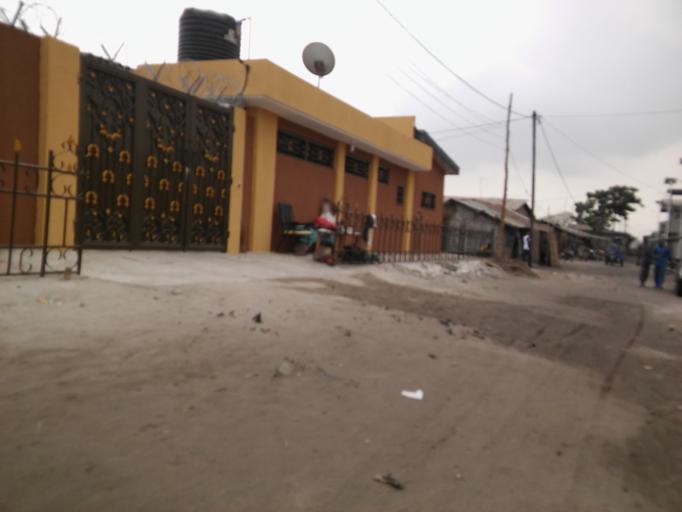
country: BJ
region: Littoral
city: Cotonou
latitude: 6.3881
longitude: 2.4229
